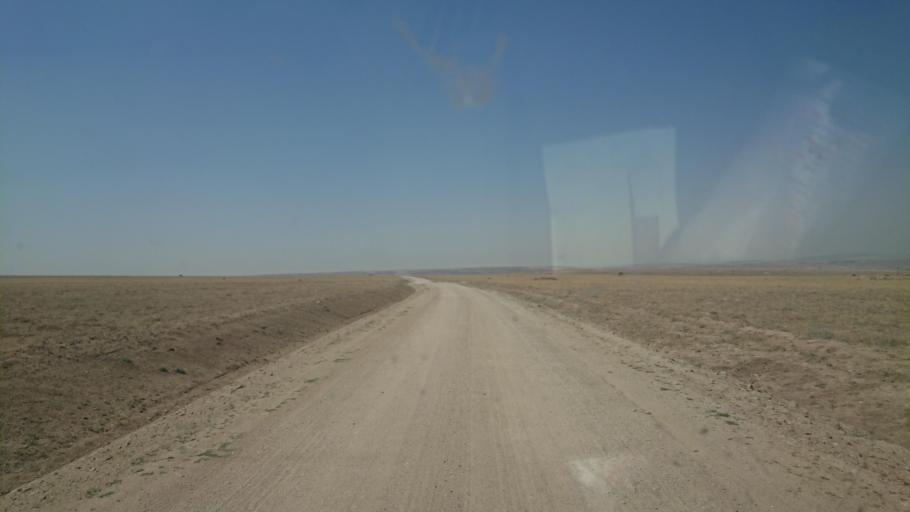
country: TR
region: Aksaray
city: Agacoren
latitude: 38.7466
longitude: 33.8996
